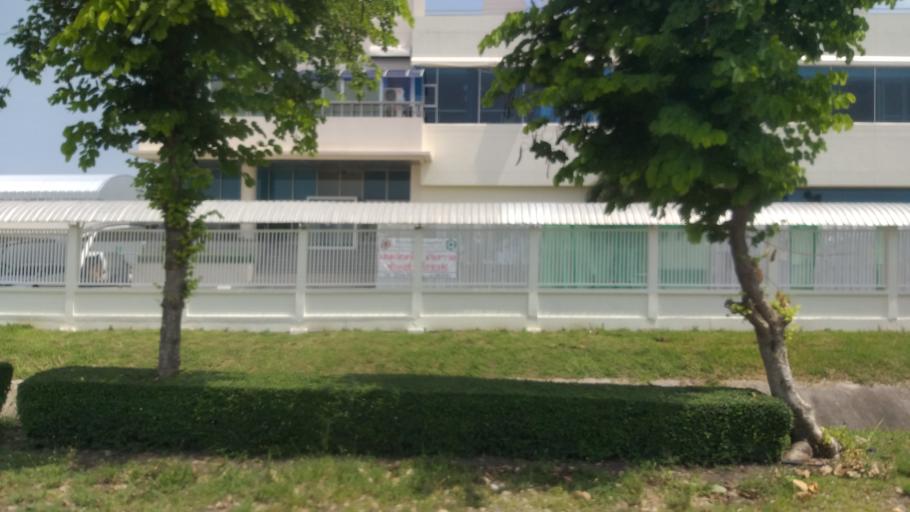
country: TH
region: Bangkok
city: Lat Krabang
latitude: 13.7138
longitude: 100.7656
